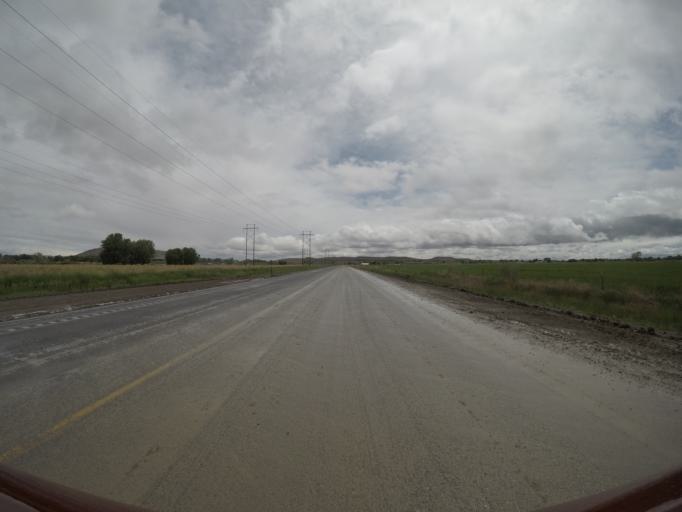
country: US
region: Wyoming
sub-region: Big Horn County
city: Lovell
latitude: 44.8509
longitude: -108.3316
